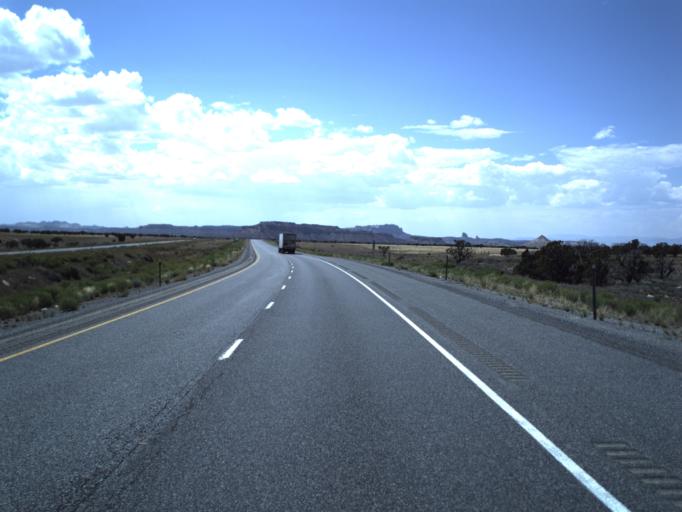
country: US
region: Utah
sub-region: Emery County
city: Castle Dale
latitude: 38.8975
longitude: -110.5976
